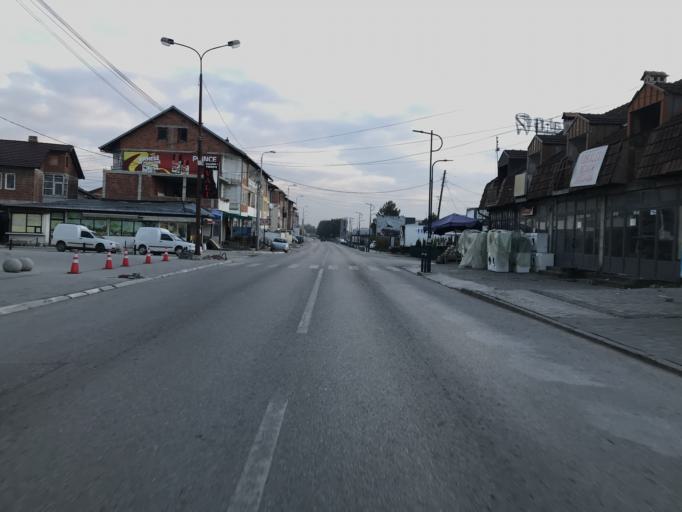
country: XK
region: Pec
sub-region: Komuna e Pejes
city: Peje
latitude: 42.6542
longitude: 20.3020
